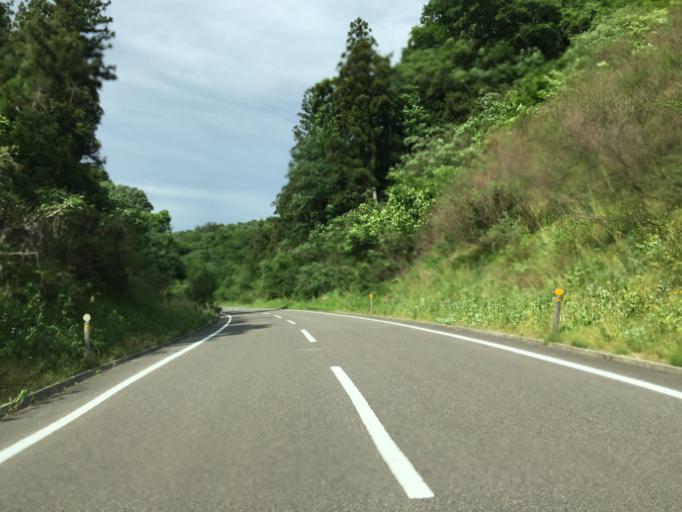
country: JP
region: Fukushima
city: Nihommatsu
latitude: 37.6031
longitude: 140.5206
